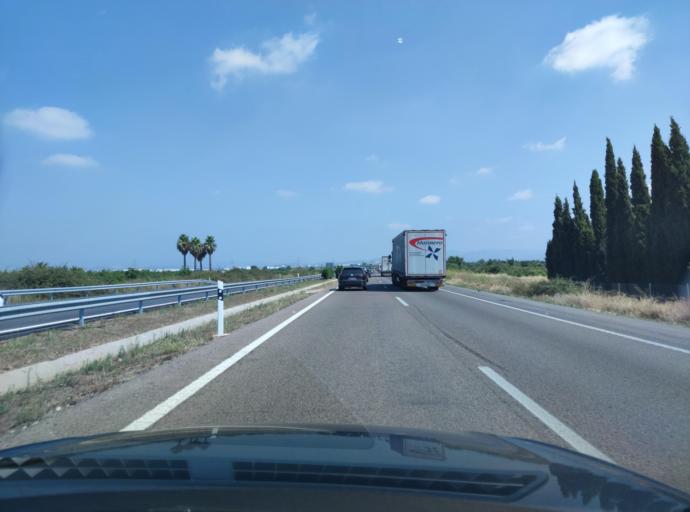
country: ES
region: Valencia
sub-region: Provincia de Castello
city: Alquerias del Nino Perdido
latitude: 39.9109
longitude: -0.1354
